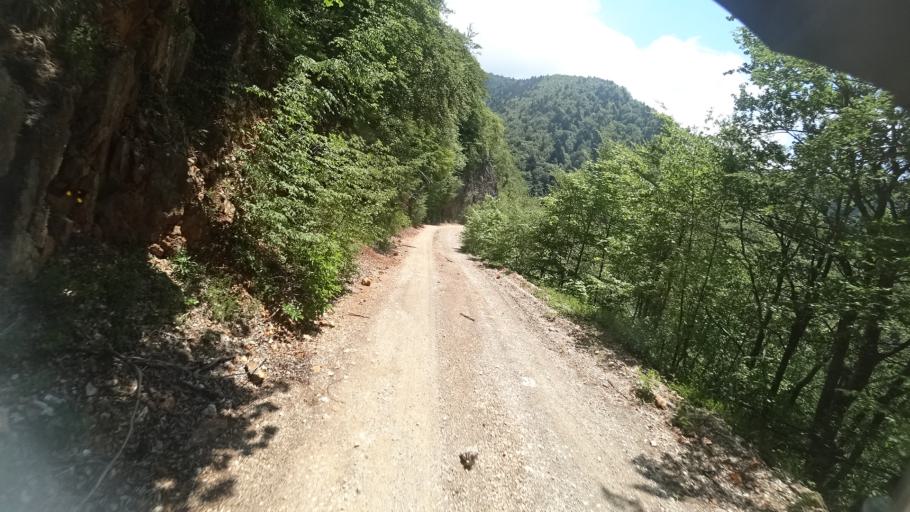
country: BA
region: Federation of Bosnia and Herzegovina
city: Orasac
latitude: 44.5773
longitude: 15.8574
